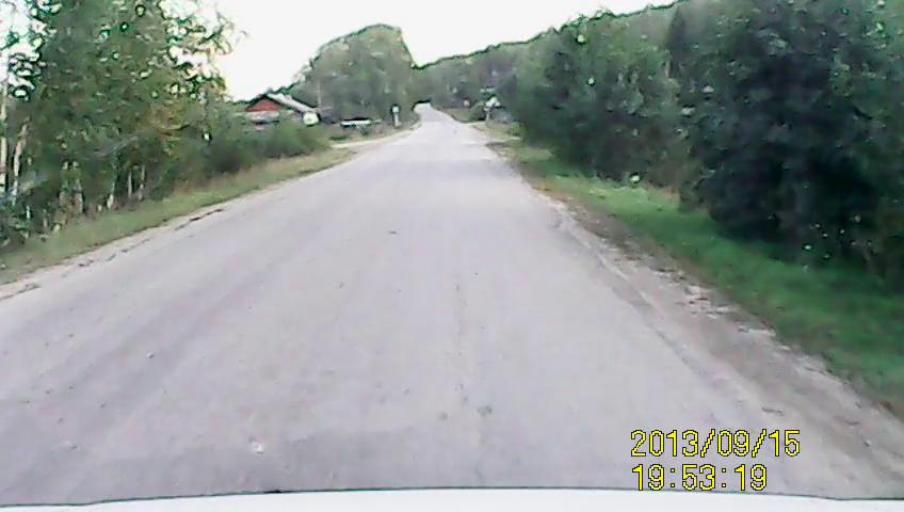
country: RU
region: Chelyabinsk
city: Kyshtym
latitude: 55.7647
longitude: 60.4857
